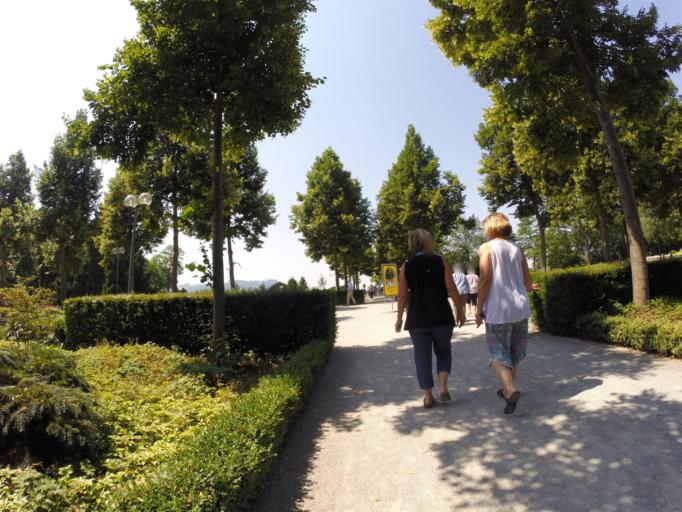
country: CH
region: Bern
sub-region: Bern-Mittelland District
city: Bern
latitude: 46.9519
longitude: 7.4608
